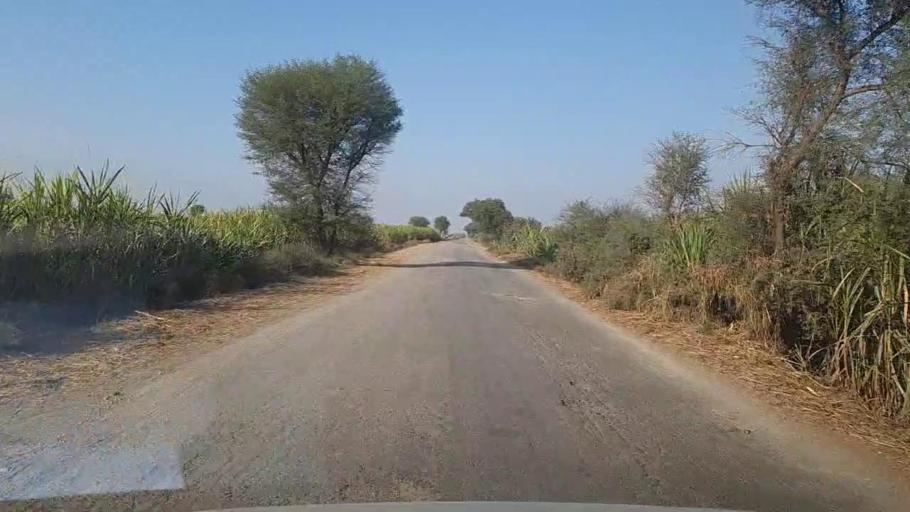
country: PK
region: Sindh
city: Phulji
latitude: 26.8507
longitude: 67.7937
